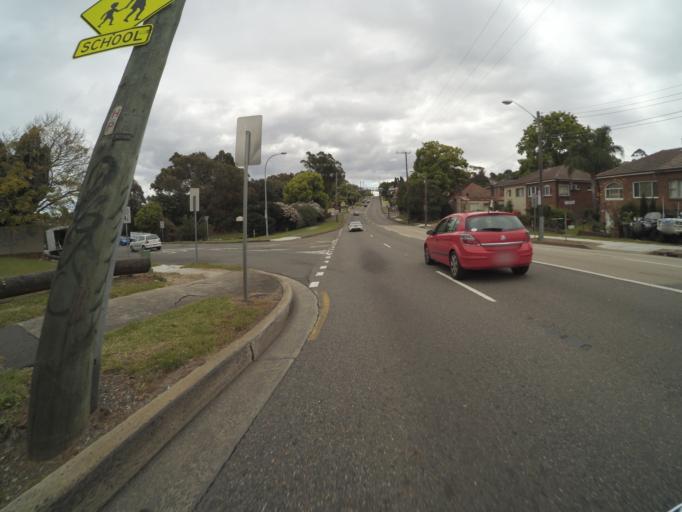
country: AU
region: New South Wales
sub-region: Kogarah
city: Hurstville Grove
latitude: -33.9740
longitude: 151.1017
